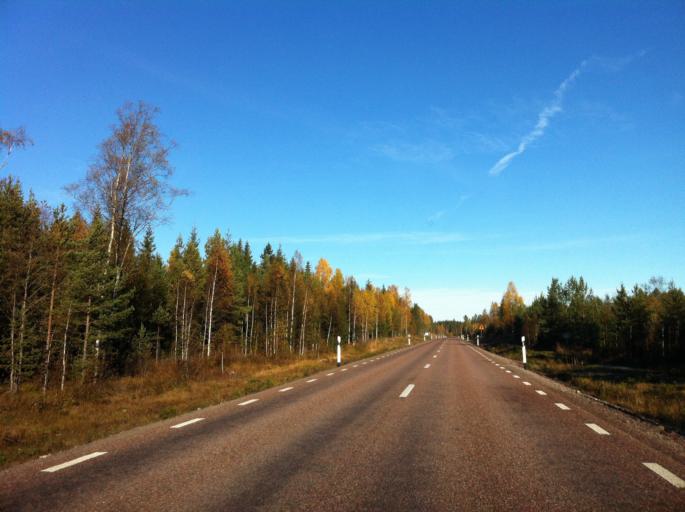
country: SE
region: Gaevleborg
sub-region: Gavle Kommun
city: Gavle
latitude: 60.6052
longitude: 17.1218
